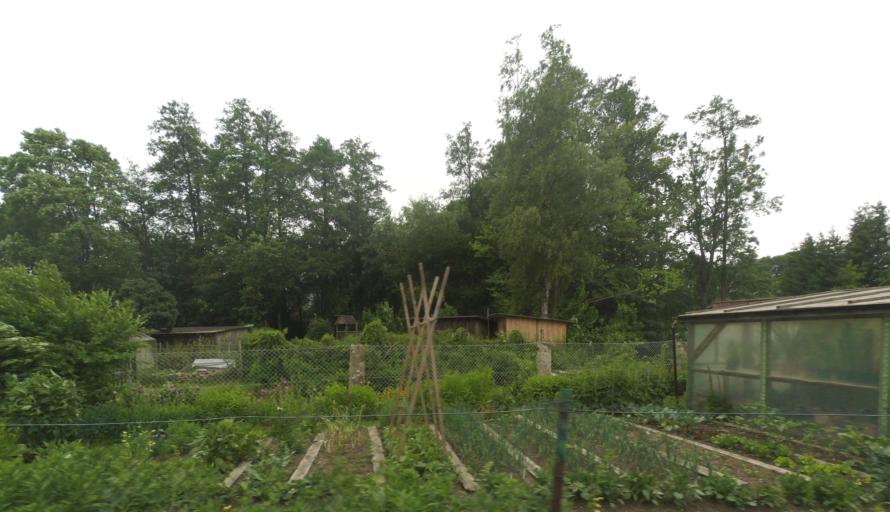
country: DE
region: Bavaria
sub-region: Upper Franconia
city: Weissenstadt
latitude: 50.0997
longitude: 11.8855
